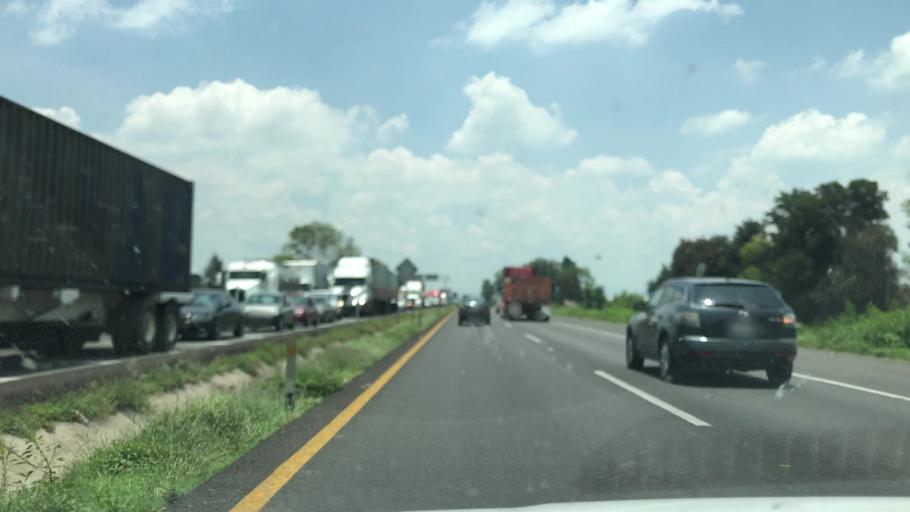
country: MX
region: Guanajuato
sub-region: Irapuato
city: Colonia Morelos de Guadalupe de Rivera
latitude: 20.6049
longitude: -101.4134
